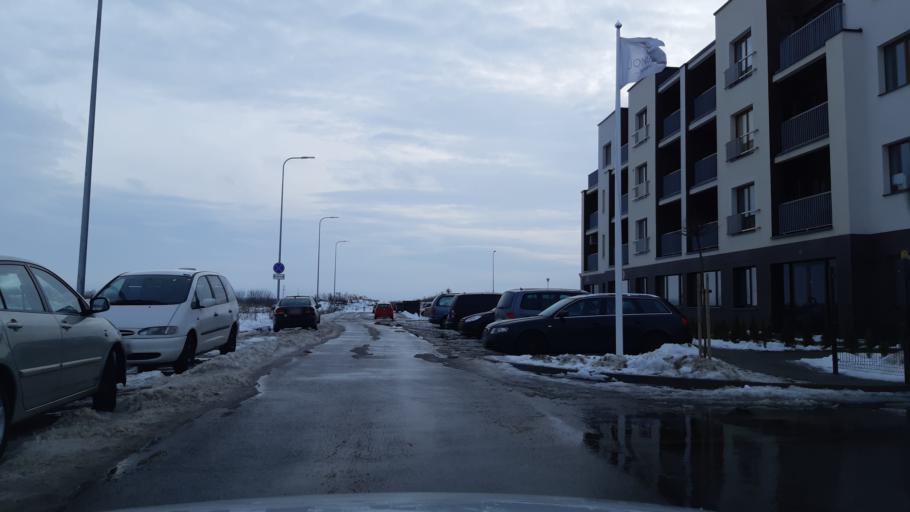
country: LT
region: Kauno apskritis
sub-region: Kauno rajonas
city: Garliava
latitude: 54.8375
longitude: 23.9059
